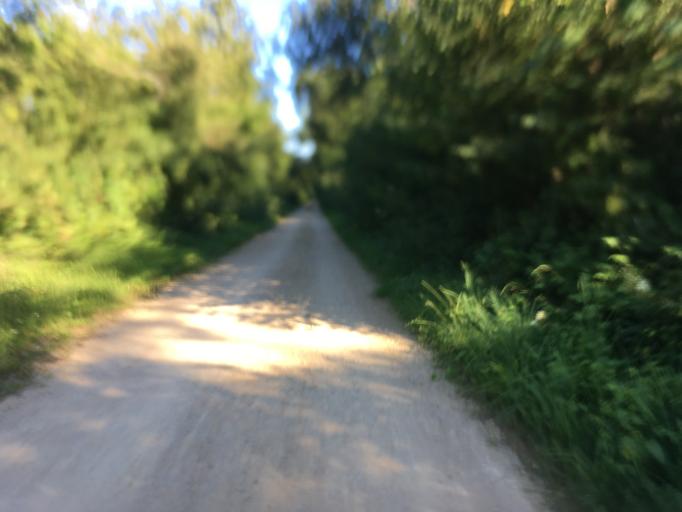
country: CH
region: Fribourg
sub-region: See District
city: Bas-Vully
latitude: 46.9529
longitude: 7.1290
